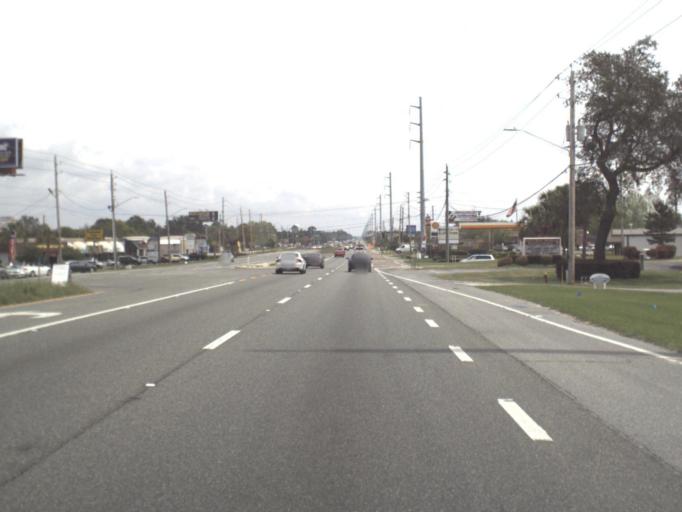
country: US
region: Florida
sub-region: Santa Rosa County
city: Oriole Beach
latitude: 30.3858
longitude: -87.0932
